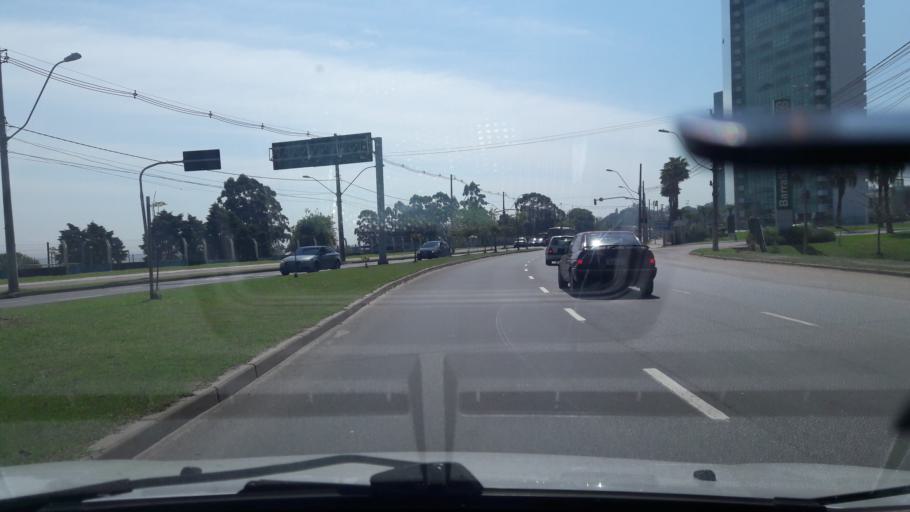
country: BR
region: Rio Grande do Sul
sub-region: Porto Alegre
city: Porto Alegre
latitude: -30.0884
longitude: -51.2481
